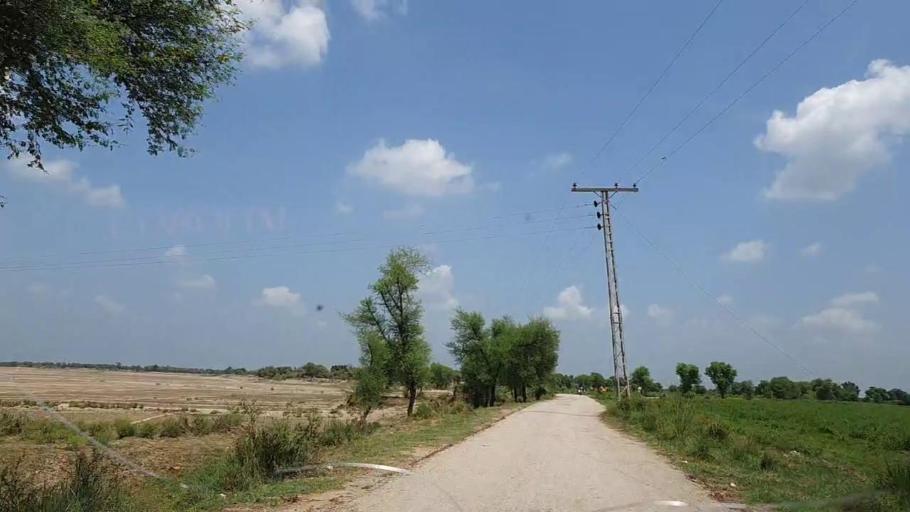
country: PK
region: Sindh
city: Tharu Shah
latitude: 27.0021
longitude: 68.0599
